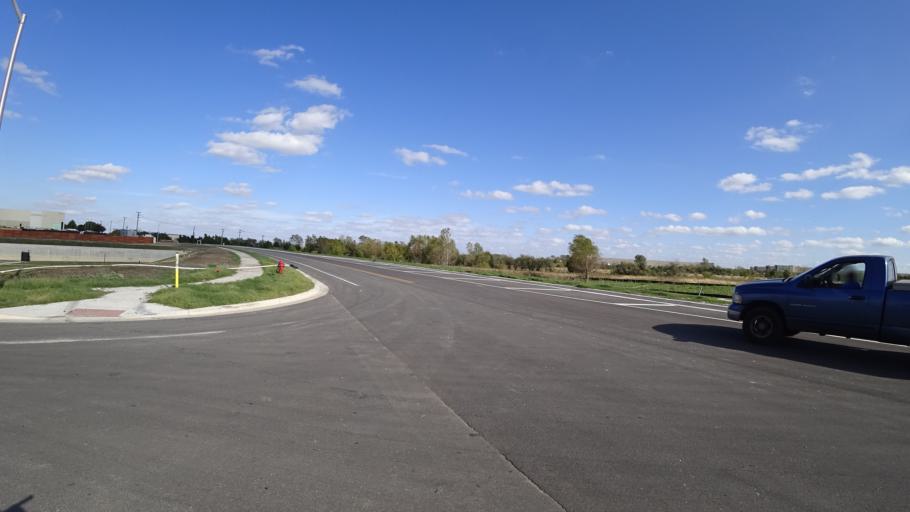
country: US
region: Texas
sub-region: Travis County
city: Wells Branch
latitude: 30.4650
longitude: -97.6785
